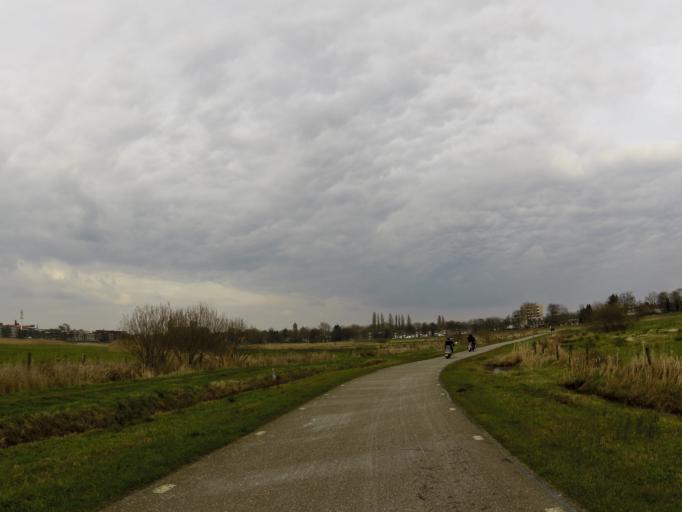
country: NL
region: North Brabant
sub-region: Gemeente 's-Hertogenbosch
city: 's-Hertogenbosch
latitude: 51.6784
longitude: 5.3059
